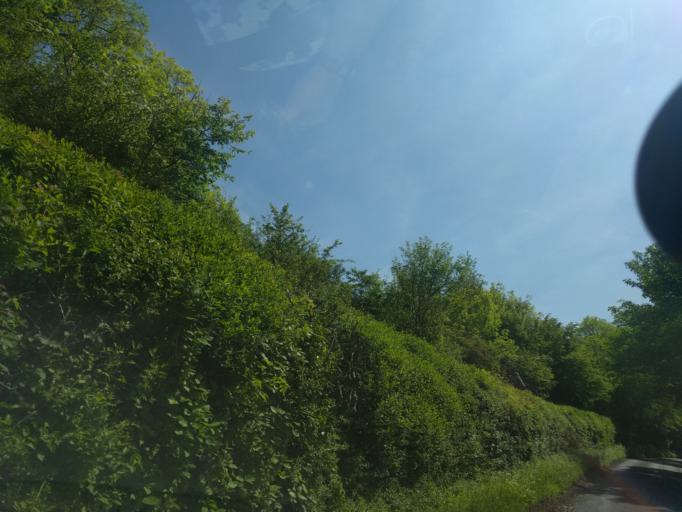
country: GB
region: England
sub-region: Somerset
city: Langport
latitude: 51.0836
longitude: -2.8180
